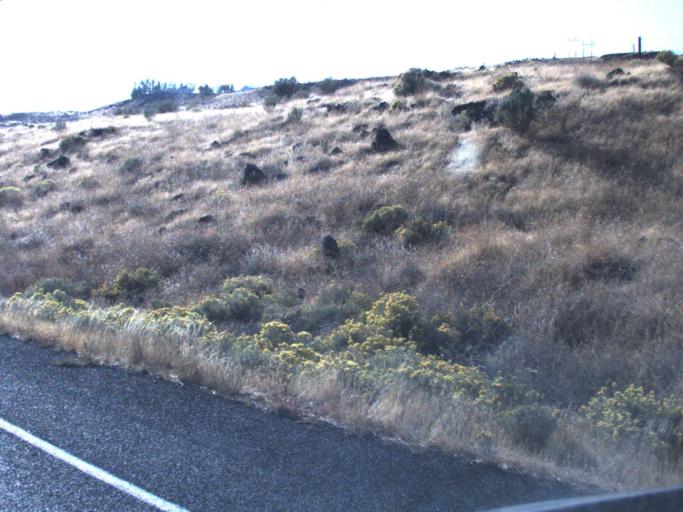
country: US
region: Oregon
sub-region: Morrow County
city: Boardman
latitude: 45.8654
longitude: -119.8513
